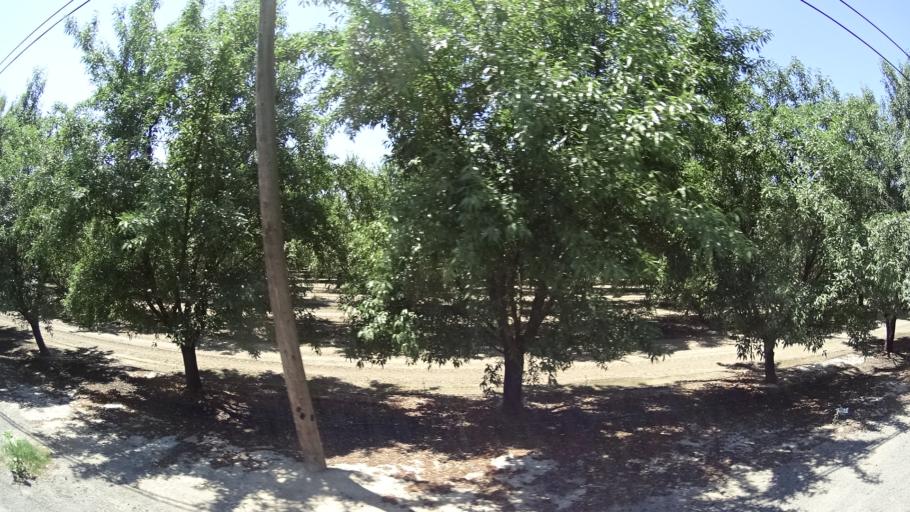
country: US
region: California
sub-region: Kings County
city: Lucerne
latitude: 36.3859
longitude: -119.6551
